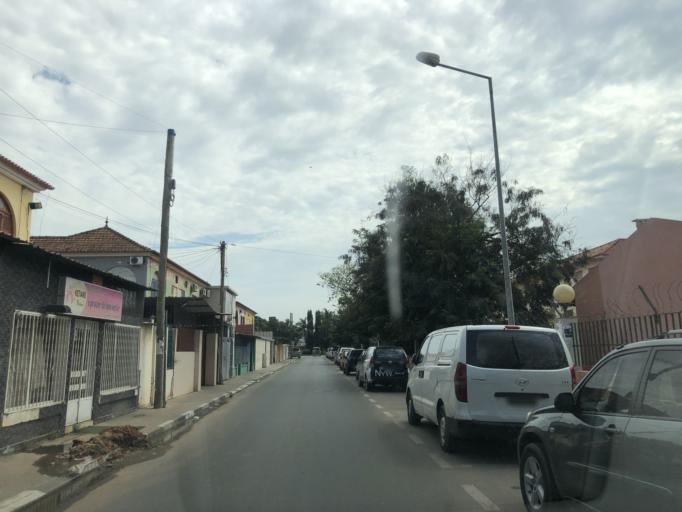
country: AO
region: Luanda
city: Luanda
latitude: -8.8246
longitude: 13.2481
